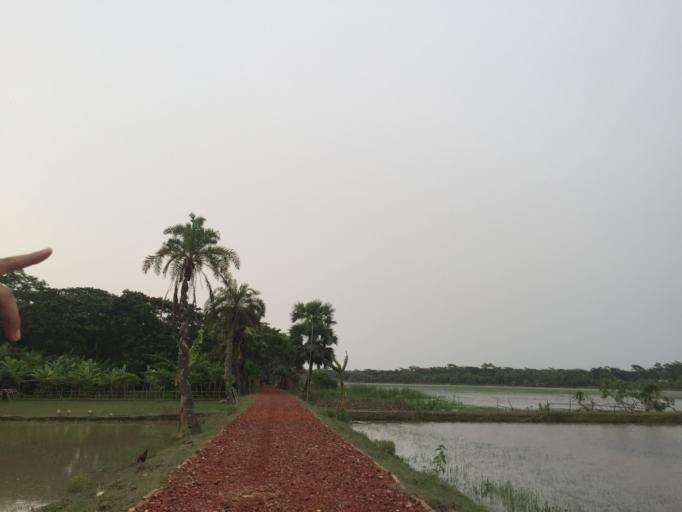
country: BD
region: Barisal
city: Mathba
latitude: 22.1938
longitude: 89.9323
